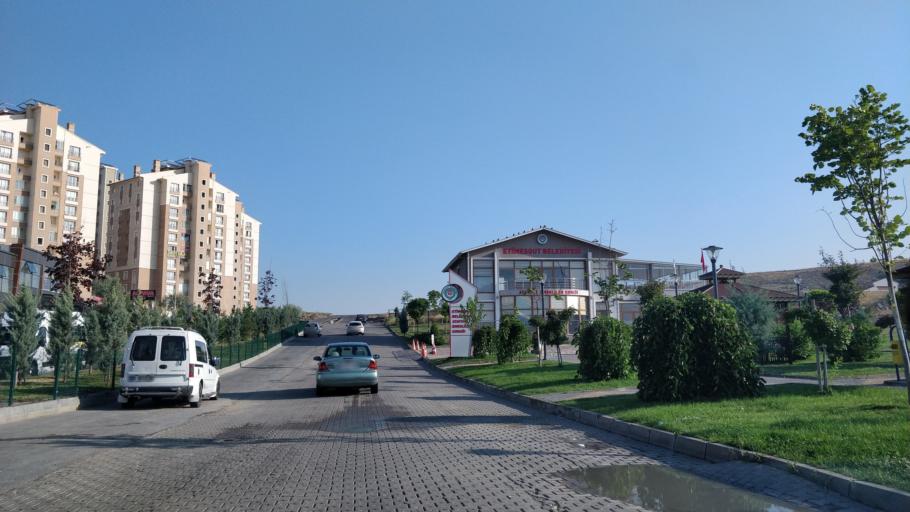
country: TR
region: Ankara
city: Etimesgut
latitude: 39.8434
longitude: 32.5466
